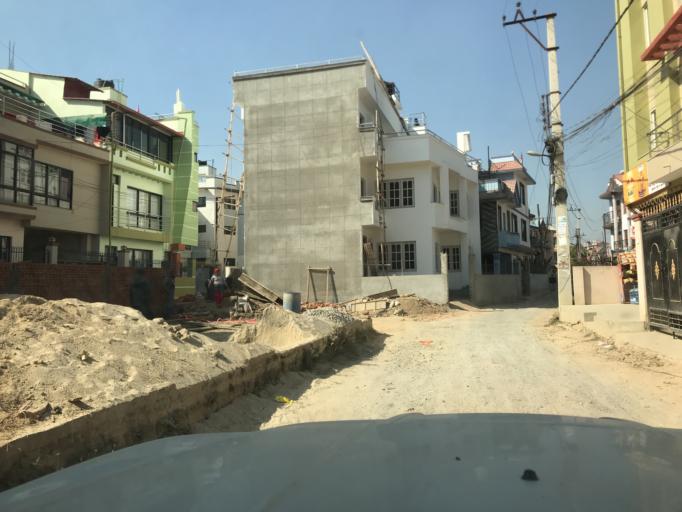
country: NP
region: Central Region
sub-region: Bagmati Zone
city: Patan
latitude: 27.6437
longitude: 85.3189
